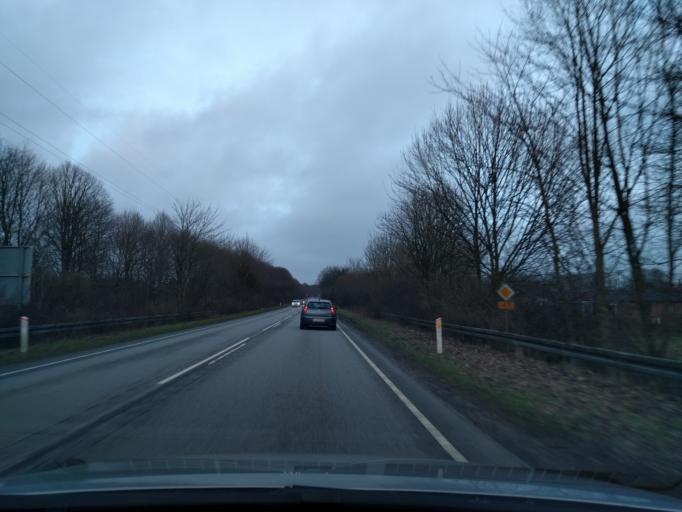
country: DK
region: South Denmark
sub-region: Haderslev Kommune
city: Vojens
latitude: 55.2494
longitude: 9.2939
